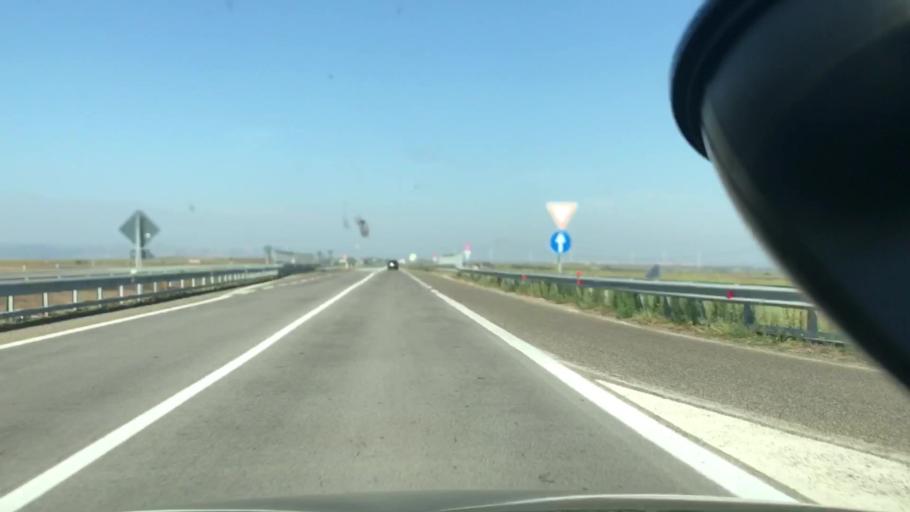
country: IT
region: Basilicate
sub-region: Provincia di Potenza
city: Venosa
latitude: 40.9936
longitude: 15.8885
